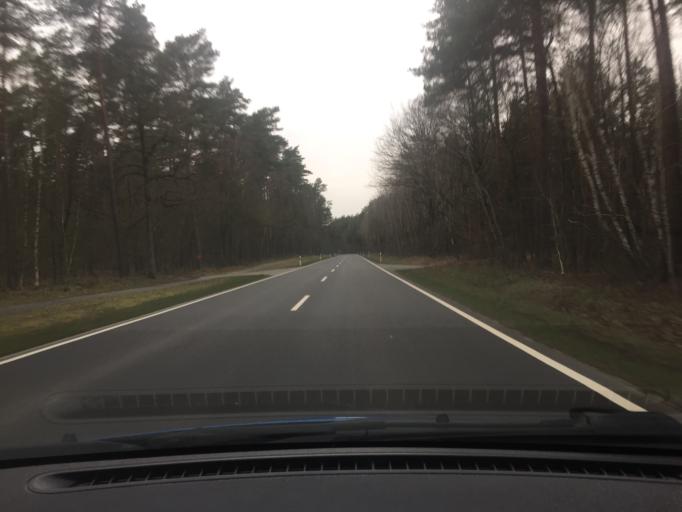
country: DE
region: Lower Saxony
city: Kusten
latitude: 52.9813
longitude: 11.0343
